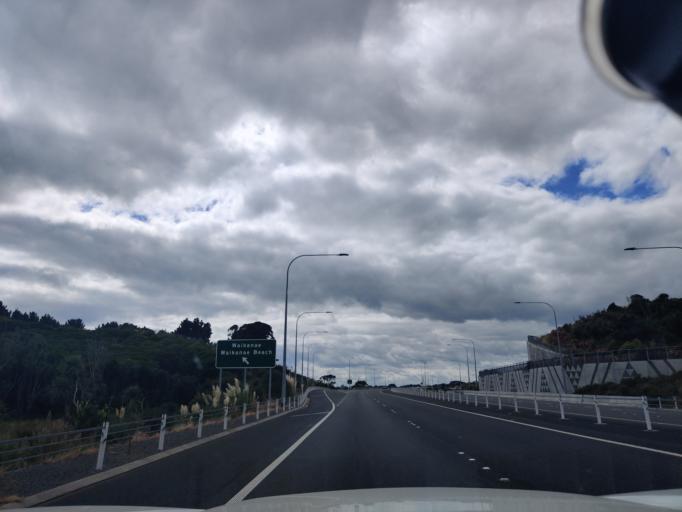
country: NZ
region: Wellington
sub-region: Kapiti Coast District
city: Paraparaumu
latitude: -40.8723
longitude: 175.0304
